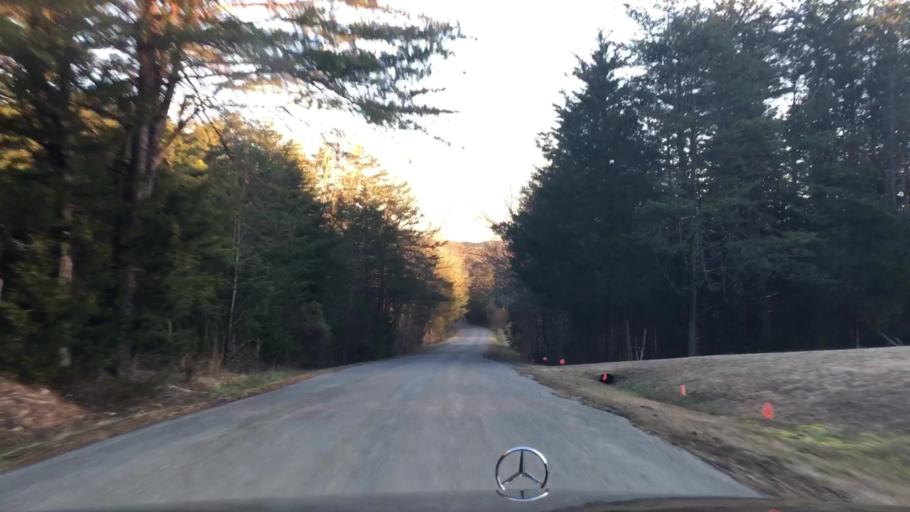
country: US
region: Virginia
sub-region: Campbell County
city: Altavista
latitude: 37.1836
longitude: -79.2957
